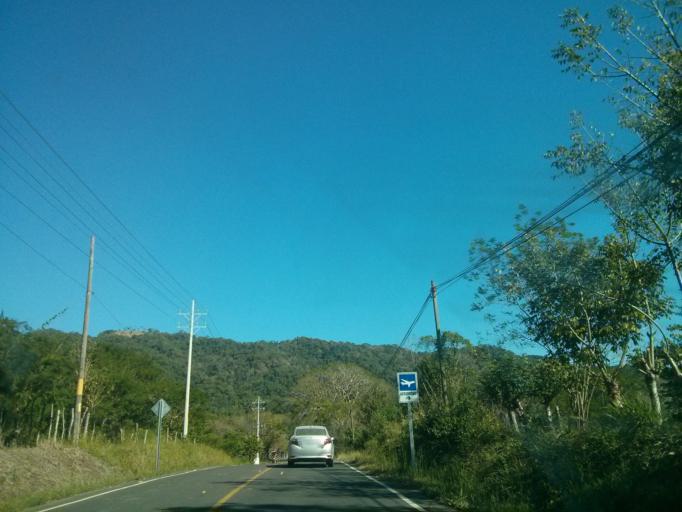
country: CR
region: Puntarenas
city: Paquera
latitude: 9.7393
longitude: -85.0195
